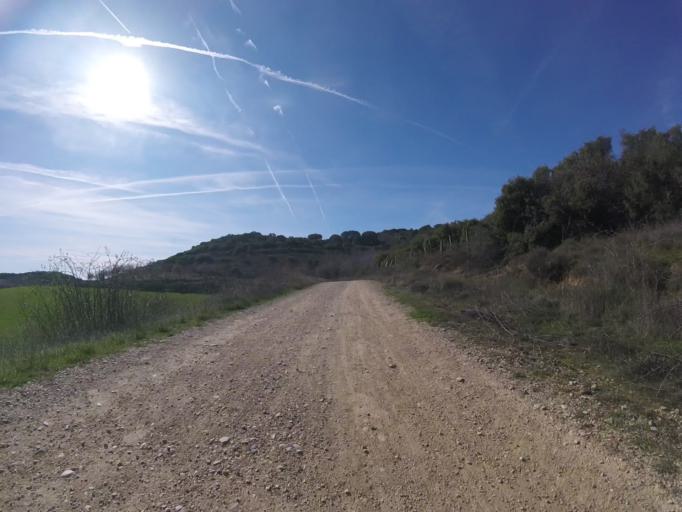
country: ES
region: Navarre
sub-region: Provincia de Navarra
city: Cirauqui
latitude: 42.6335
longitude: -1.8887
